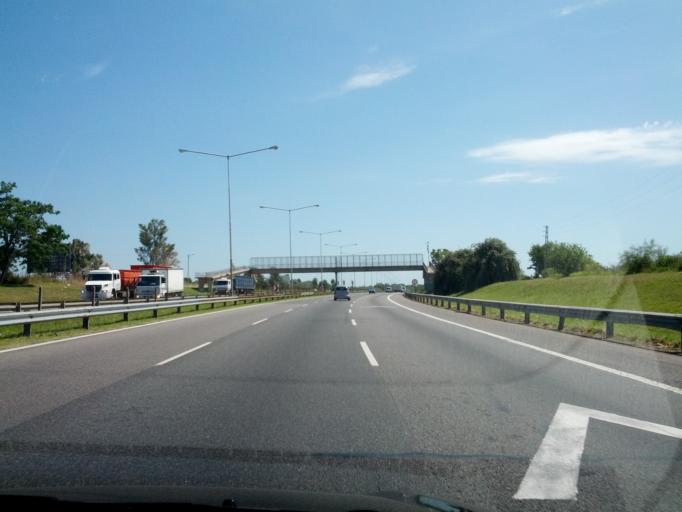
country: AR
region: Buenos Aires
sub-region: Partido de Campana
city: Campana
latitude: -34.2491
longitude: -58.9079
